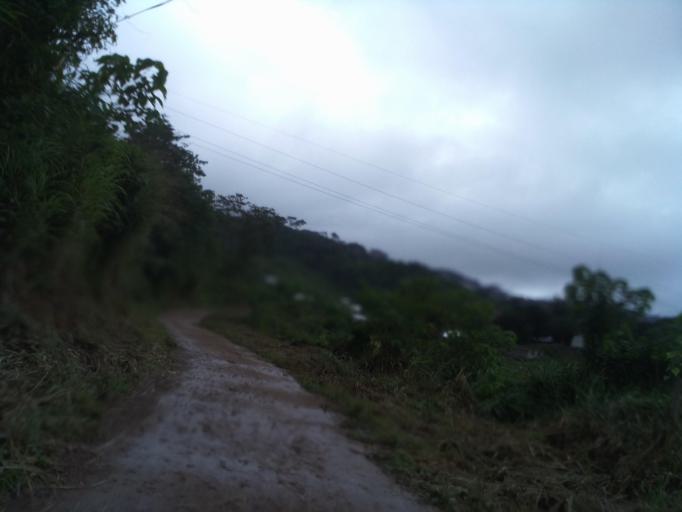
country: SL
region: Eastern Province
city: Kenema
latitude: 7.8548
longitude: -11.2063
